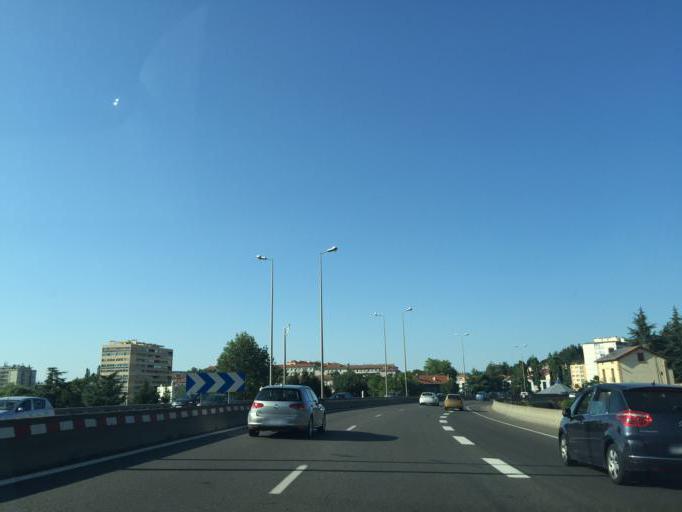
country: FR
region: Rhone-Alpes
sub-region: Departement de la Loire
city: Saint-Etienne
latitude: 45.4324
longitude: 4.4170
